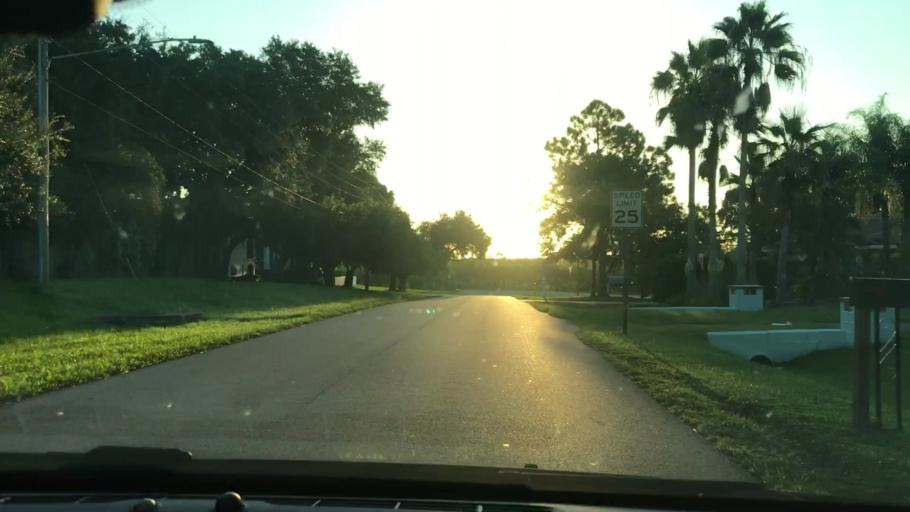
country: US
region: Florida
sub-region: Pinellas County
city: Safety Harbor
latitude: 27.9679
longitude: -82.7049
